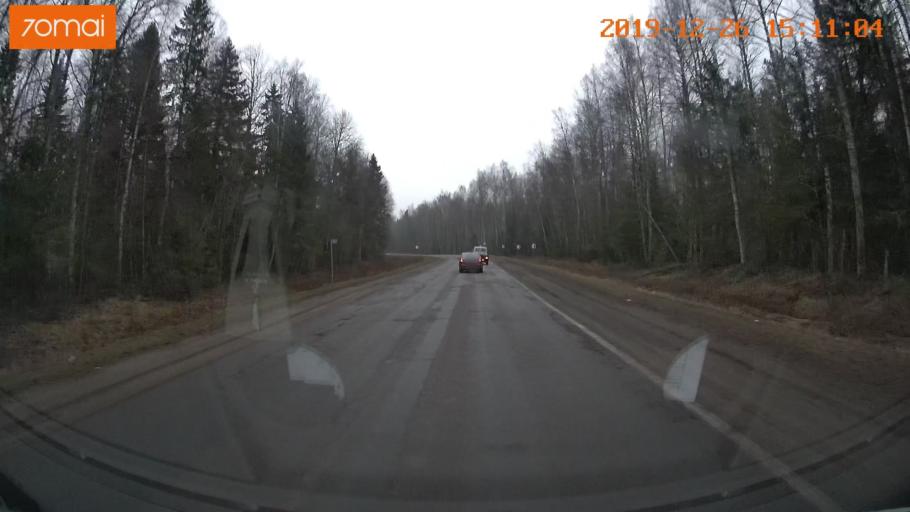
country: RU
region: Jaroslavl
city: Rybinsk
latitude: 58.1363
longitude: 38.8573
